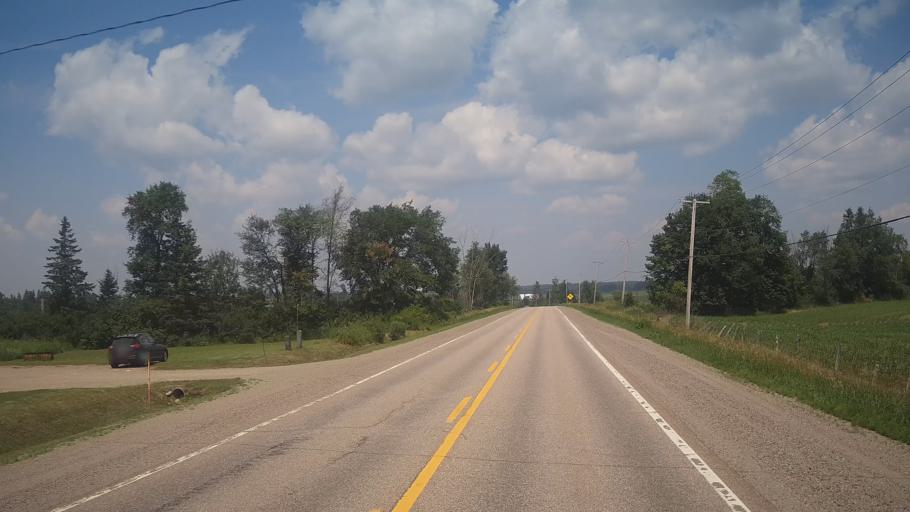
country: CA
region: Quebec
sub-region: Outaouais
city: Shawville
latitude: 45.5804
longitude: -76.4504
